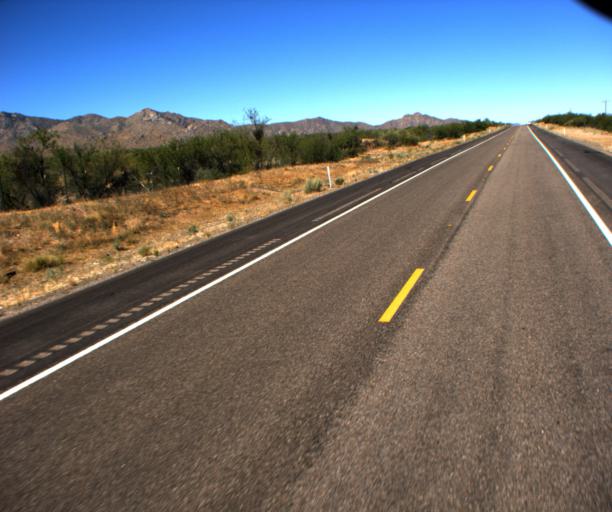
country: US
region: Arizona
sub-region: Pima County
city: Three Points
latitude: 32.0233
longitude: -111.5960
